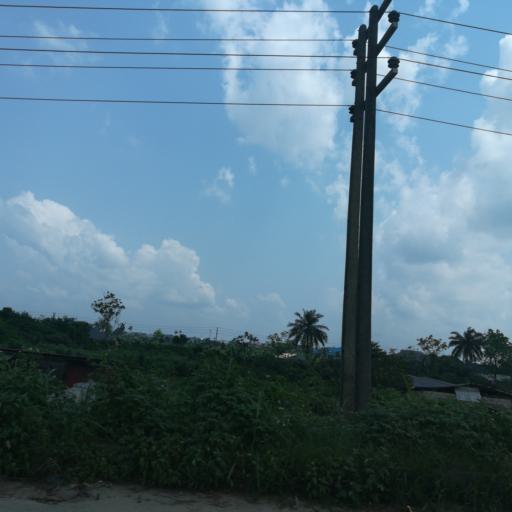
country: NG
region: Rivers
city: Port Harcourt
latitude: 4.8453
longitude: 7.0771
